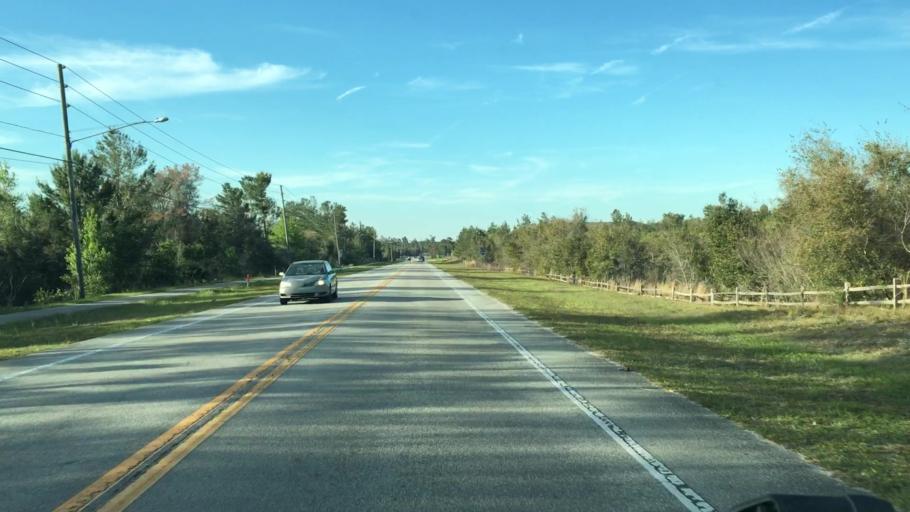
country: US
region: Florida
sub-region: Volusia County
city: Deltona
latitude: 28.9235
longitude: -81.2219
